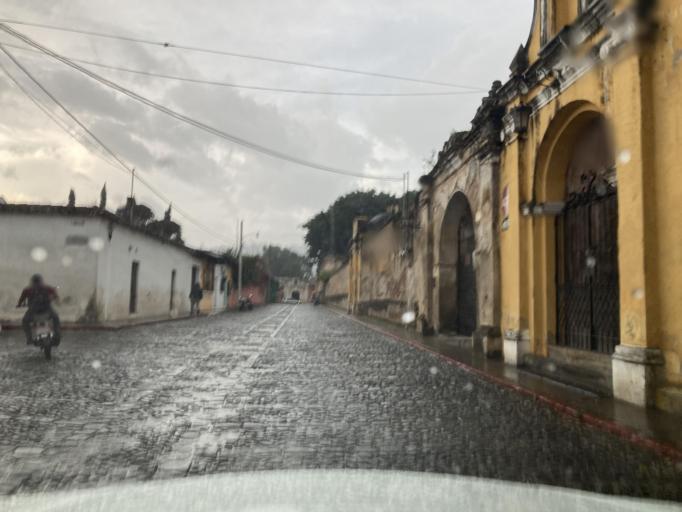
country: GT
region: Sacatepequez
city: Antigua Guatemala
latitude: 14.5532
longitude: -90.7303
